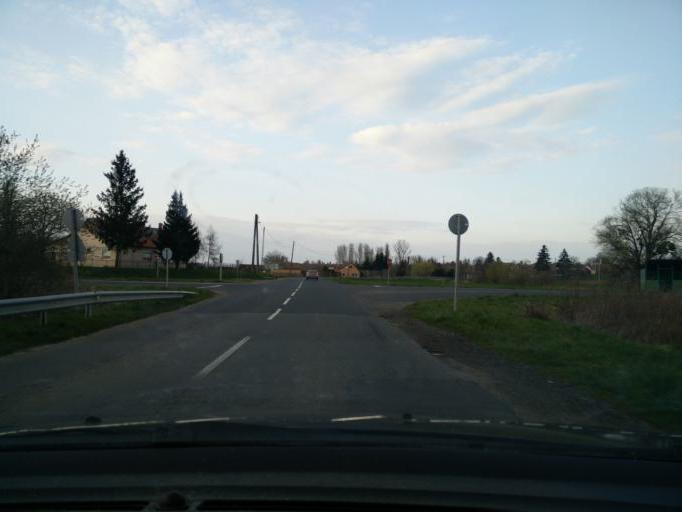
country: HU
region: Zala
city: Zalaszentgrot
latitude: 46.9828
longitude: 17.0334
